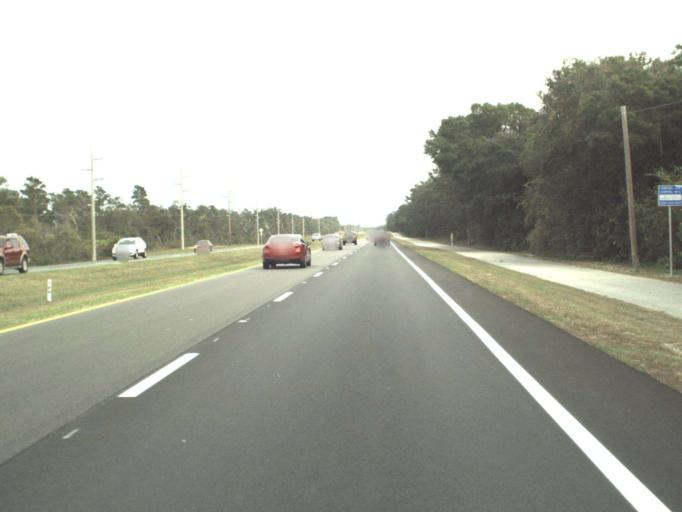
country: US
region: Florida
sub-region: Santa Rosa County
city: Gulf Breeze
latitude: 30.3606
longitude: -87.1485
